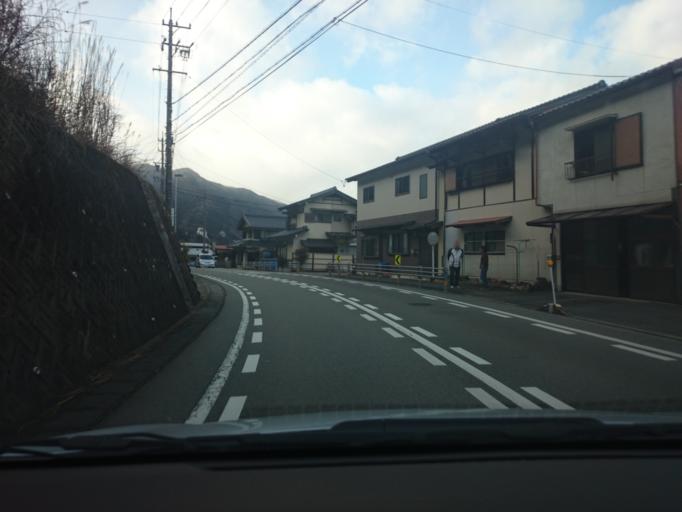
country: JP
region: Gifu
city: Gujo
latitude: 35.7970
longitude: 137.2515
